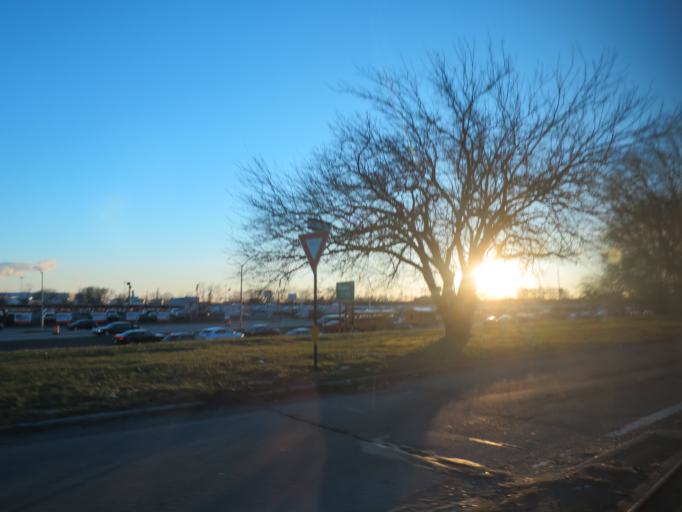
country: US
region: New York
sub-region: Queens County
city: Borough of Queens
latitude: 40.6654
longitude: -73.8187
